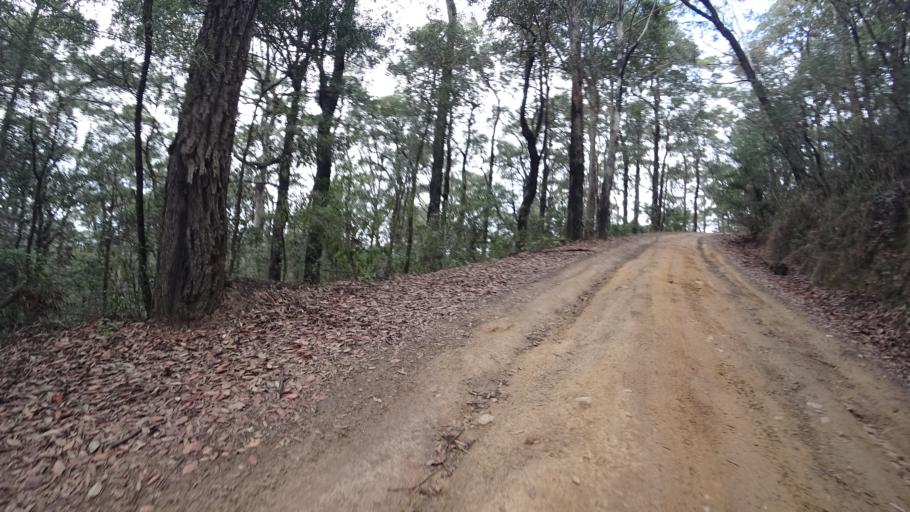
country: AU
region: New South Wales
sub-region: Shoalhaven Shire
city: Milton
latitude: -35.1730
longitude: 150.3793
